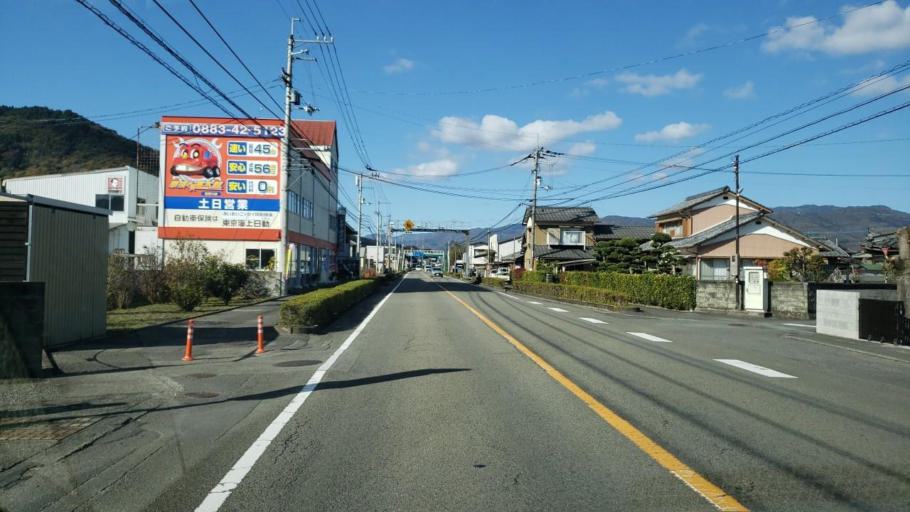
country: JP
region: Tokushima
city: Wakimachi
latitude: 34.0606
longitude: 134.2114
